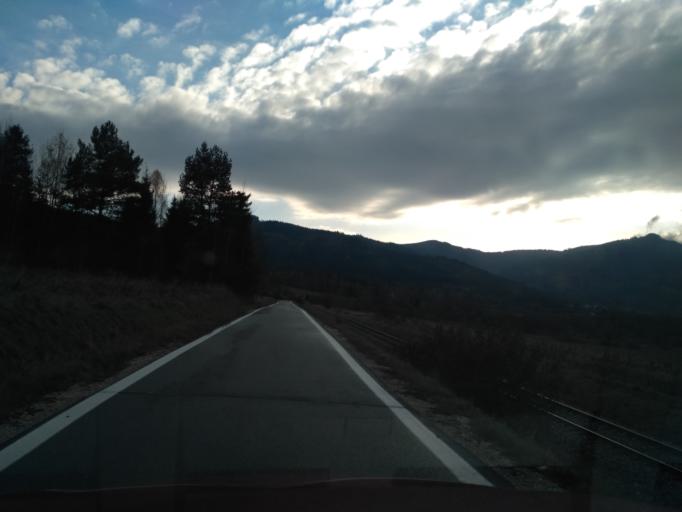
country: SK
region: Kosicky
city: Spisska Nova Ves
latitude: 48.8271
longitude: 20.6027
